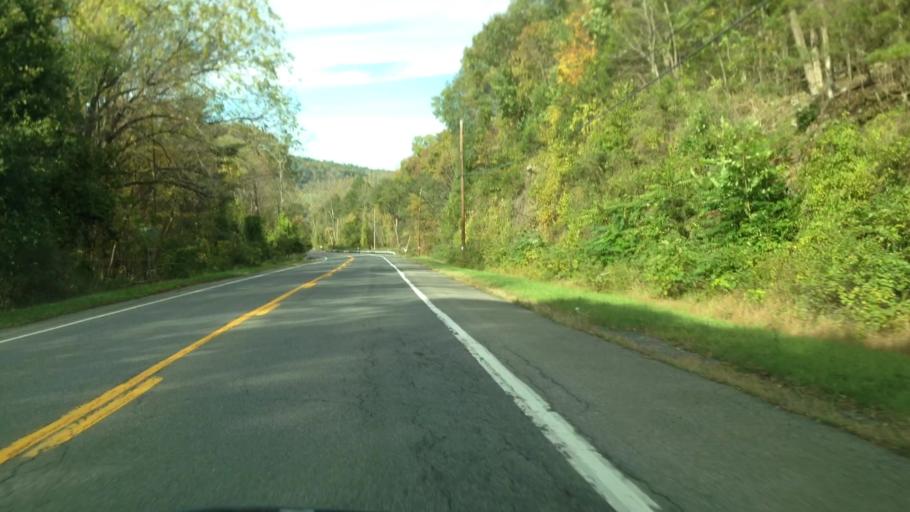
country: US
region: New York
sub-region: Ulster County
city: Port Ewen
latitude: 41.8868
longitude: -74.0163
